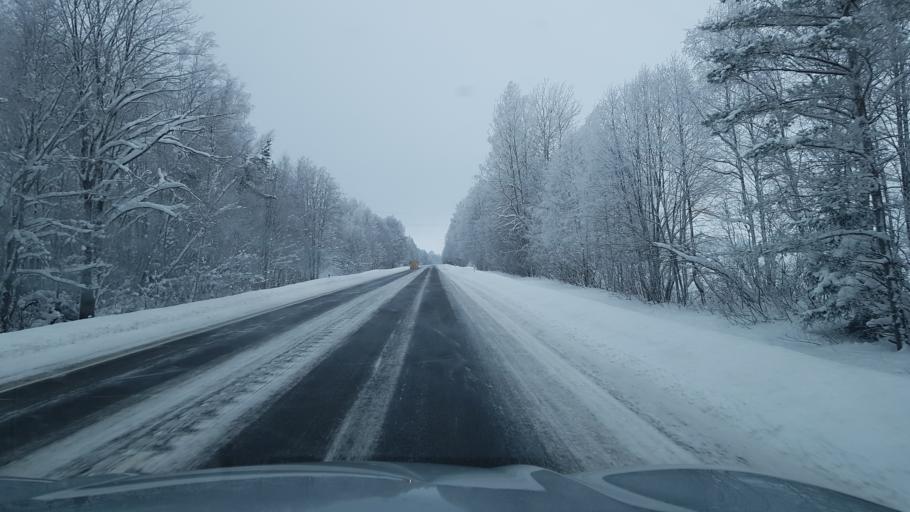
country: EE
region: Ida-Virumaa
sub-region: Johvi vald
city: Johvi
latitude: 59.2976
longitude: 27.3972
